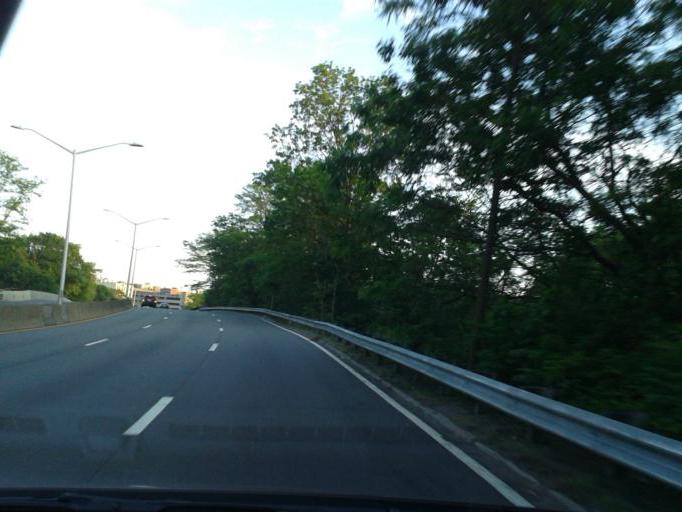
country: US
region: New York
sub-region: Westchester County
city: Mount Vernon
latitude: 40.8988
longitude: -73.8619
